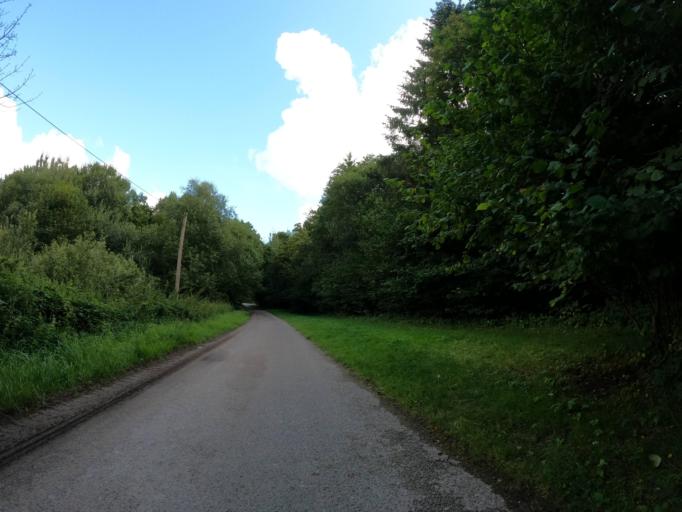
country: DE
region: Mecklenburg-Vorpommern
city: Sehlen
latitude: 54.3595
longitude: 13.4214
